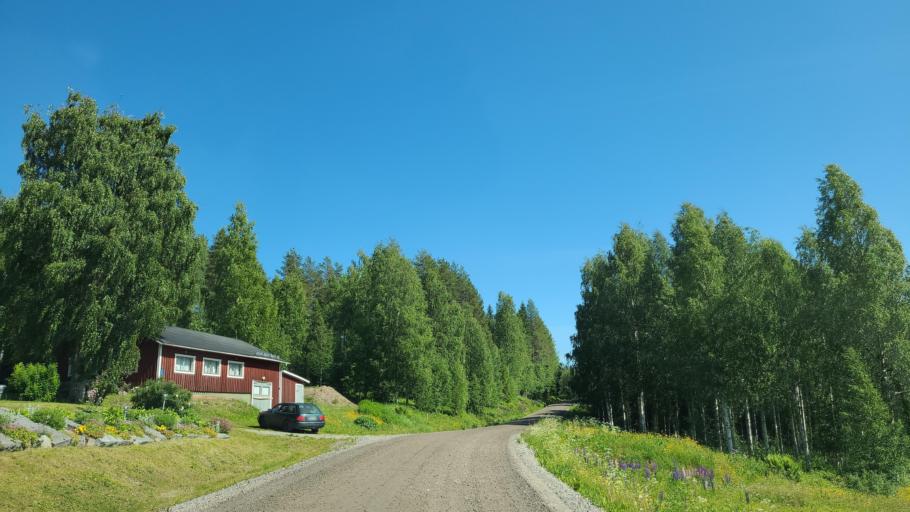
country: SE
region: Vaesterbotten
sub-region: Bjurholms Kommun
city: Bjurholm
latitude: 63.6763
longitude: 19.0469
